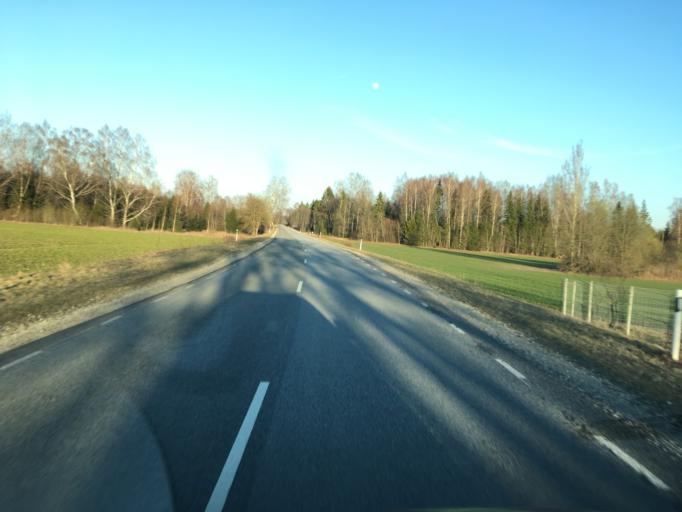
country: EE
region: Raplamaa
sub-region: Rapla vald
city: Rapla
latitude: 59.0760
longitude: 24.8718
